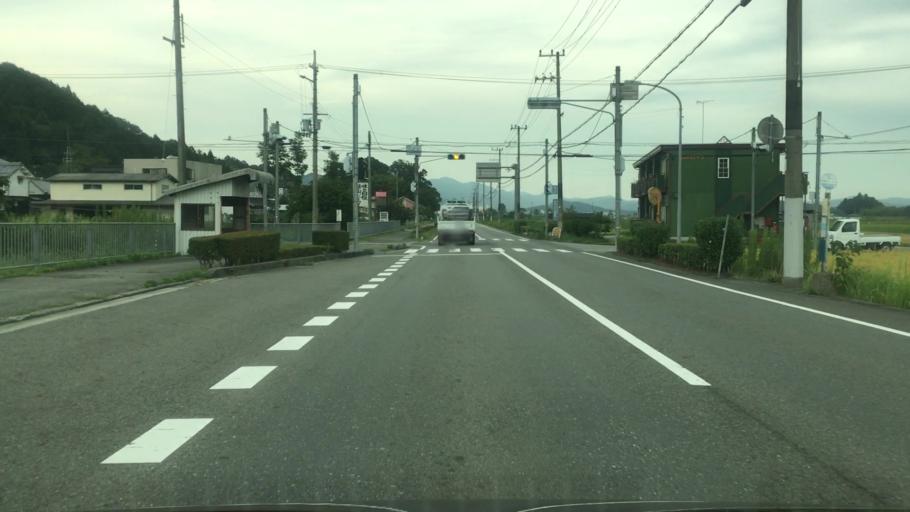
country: JP
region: Hyogo
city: Sasayama
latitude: 35.0694
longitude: 135.2611
